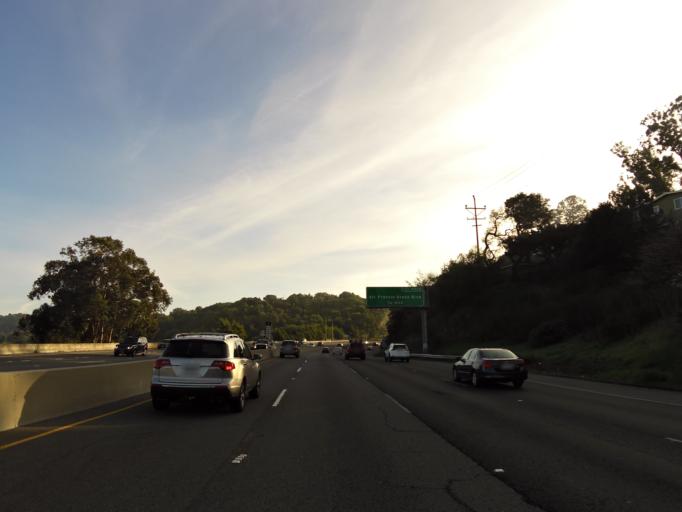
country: US
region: California
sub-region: Marin County
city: San Rafael
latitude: 37.9557
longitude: -122.5087
